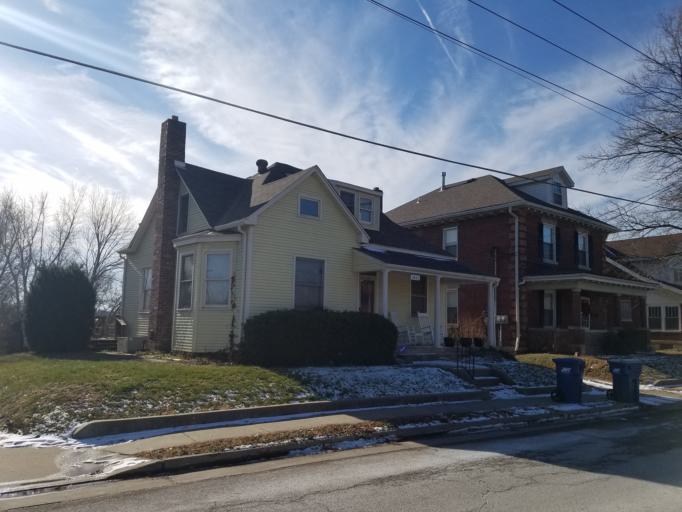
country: US
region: Missouri
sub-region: Cole County
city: Jefferson City
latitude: 38.5883
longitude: -92.1905
